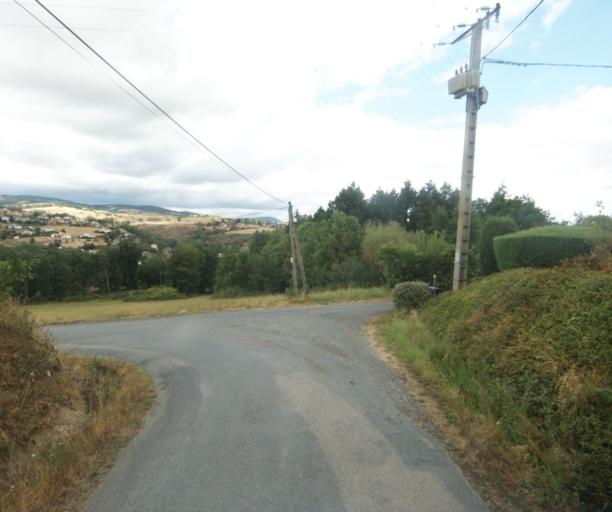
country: FR
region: Rhone-Alpes
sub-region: Departement du Rhone
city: Courzieu
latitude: 45.7472
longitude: 4.5502
